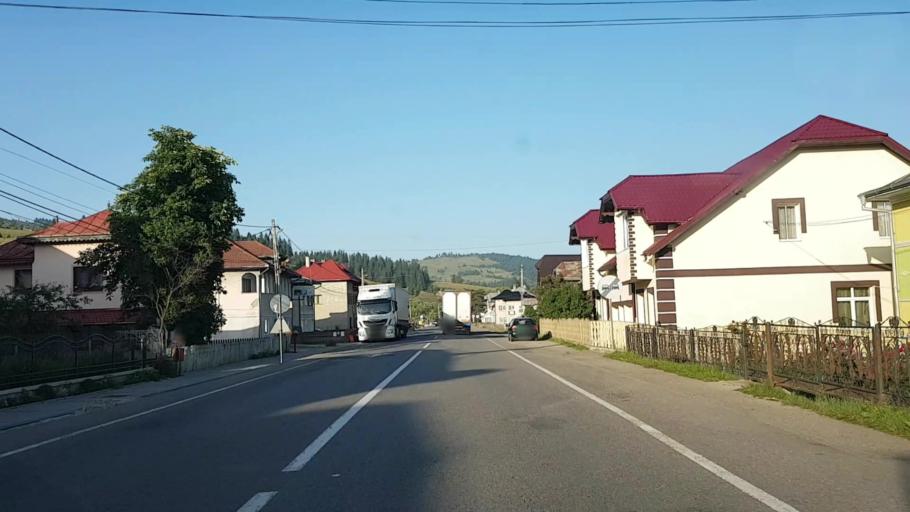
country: RO
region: Suceava
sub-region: Comuna Dorna Candrenilor
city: Dorna Candrenilor
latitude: 47.3553
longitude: 25.2663
